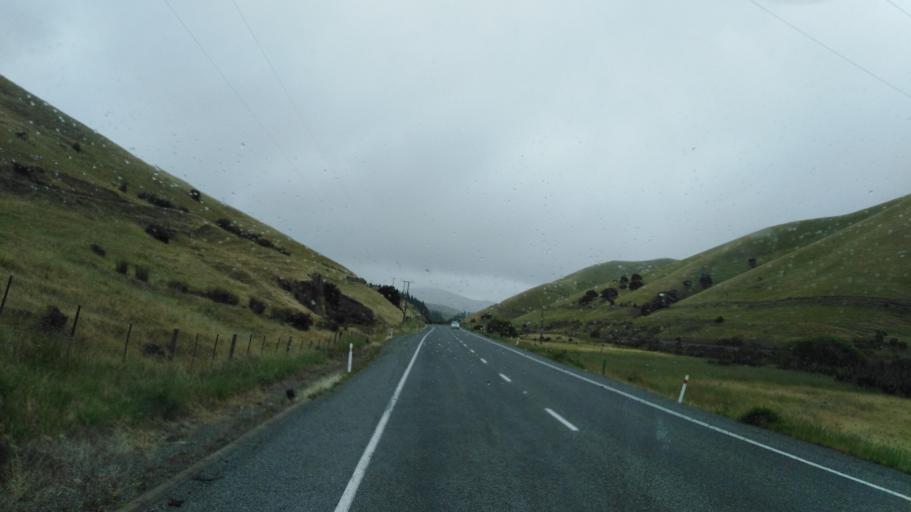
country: NZ
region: Marlborough
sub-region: Marlborough District
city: Blenheim
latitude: -41.6259
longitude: 174.0632
